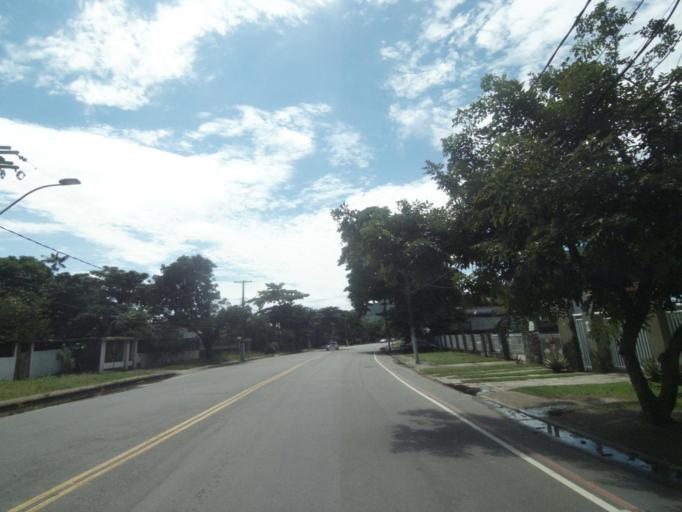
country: BR
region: Rio de Janeiro
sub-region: Niteroi
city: Niteroi
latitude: -22.9676
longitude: -43.0406
